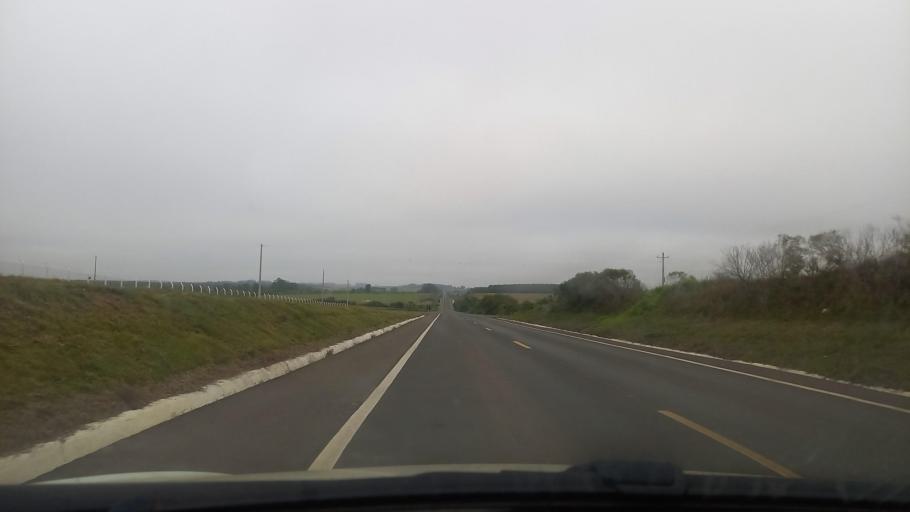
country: BR
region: Rio Grande do Sul
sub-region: Rosario Do Sul
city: Rosario do Sul
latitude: -30.2800
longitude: -54.9807
